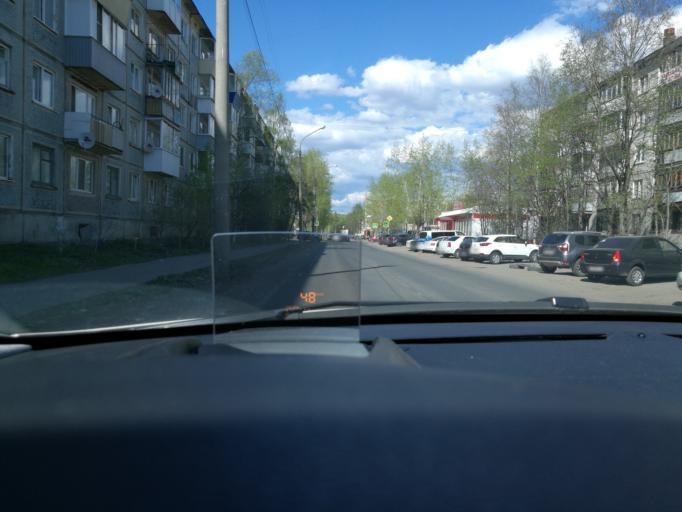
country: RU
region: Arkhangelskaya
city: Arkhangel'sk
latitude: 64.5522
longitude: 40.5370
